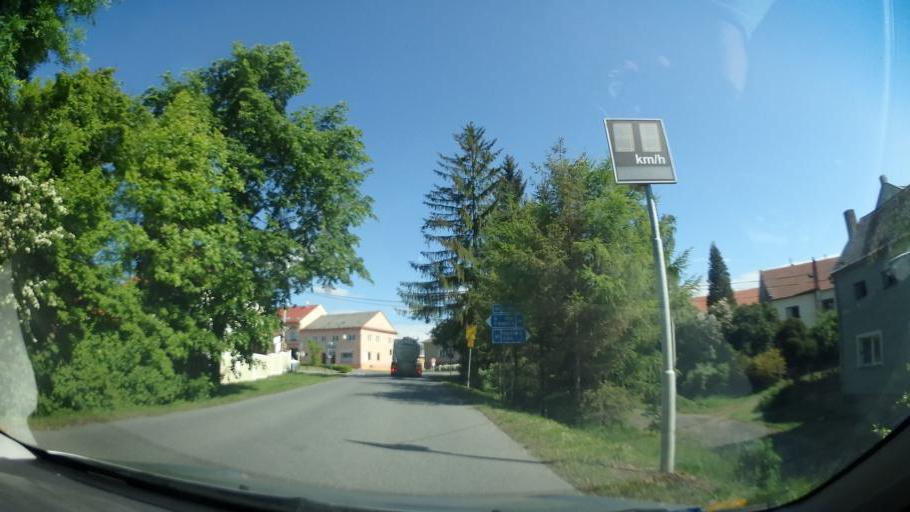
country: CZ
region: South Moravian
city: Velke Opatovice
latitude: 49.6792
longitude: 16.6295
